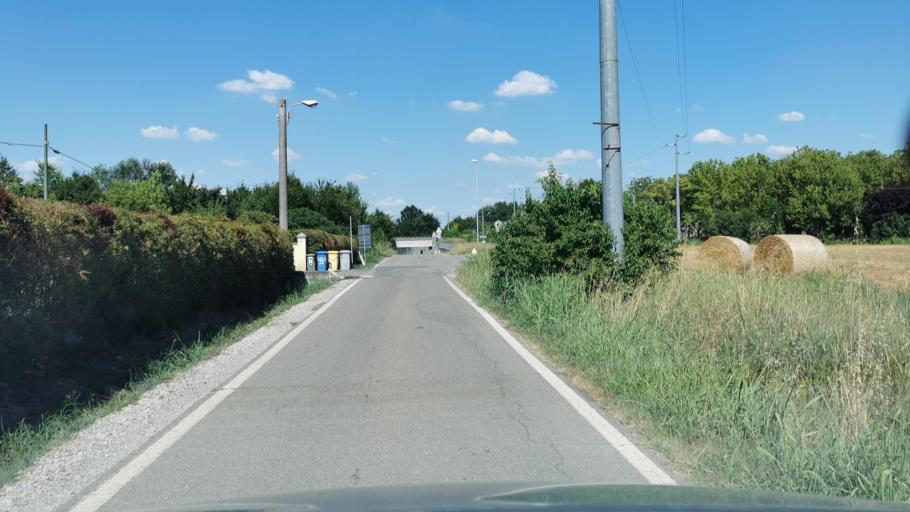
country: IT
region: Emilia-Romagna
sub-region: Provincia di Modena
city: Villanova
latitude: 44.6928
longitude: 10.9035
